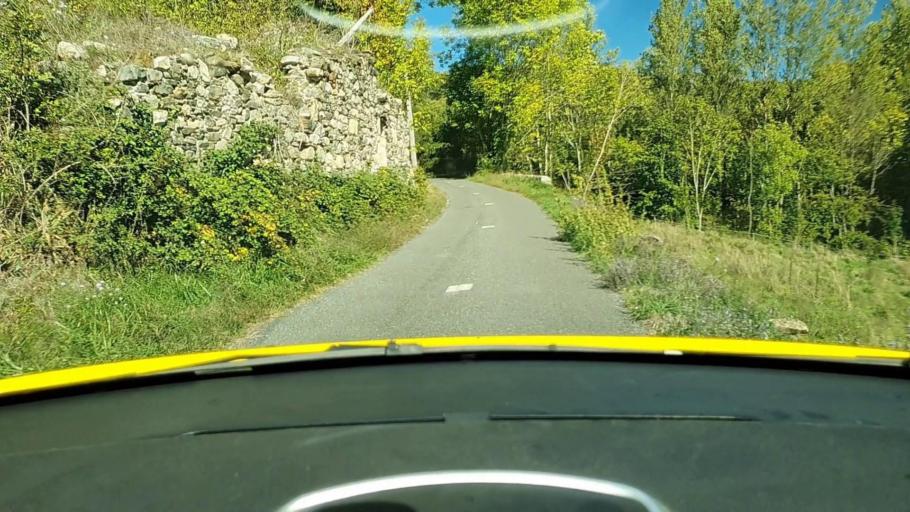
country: FR
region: Languedoc-Roussillon
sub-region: Departement du Gard
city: Le Vigan
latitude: 43.9870
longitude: 3.4489
